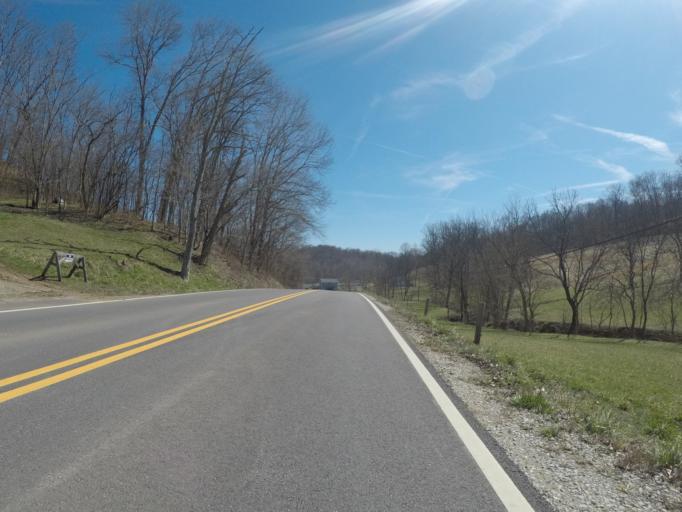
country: US
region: Ohio
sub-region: Lawrence County
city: Burlington
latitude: 38.4557
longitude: -82.5480
